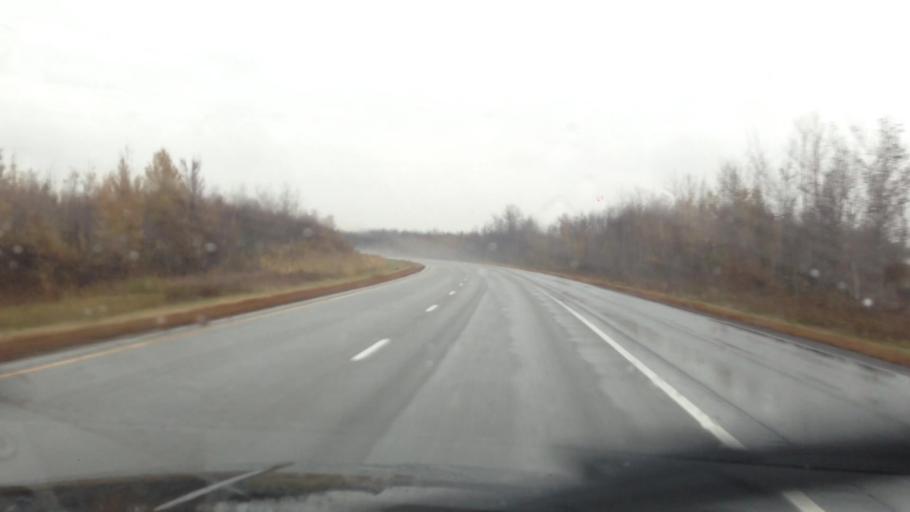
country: CA
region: Ontario
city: Casselman
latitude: 45.3066
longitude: -75.1474
